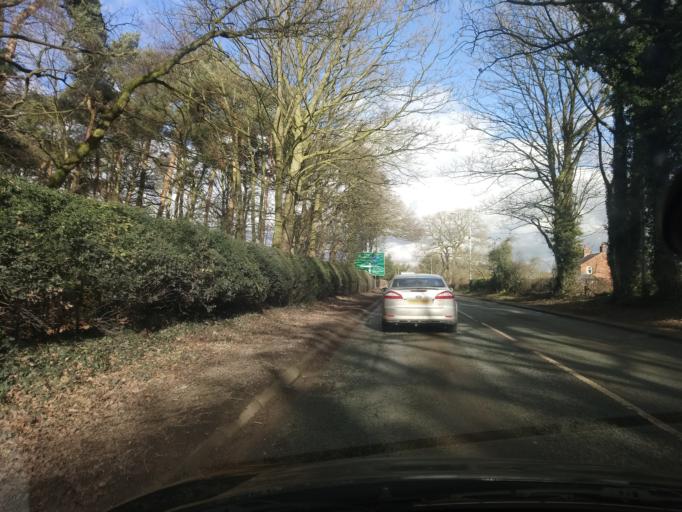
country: GB
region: England
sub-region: Cheshire West and Chester
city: Oakmere
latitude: 53.1982
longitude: -2.6324
